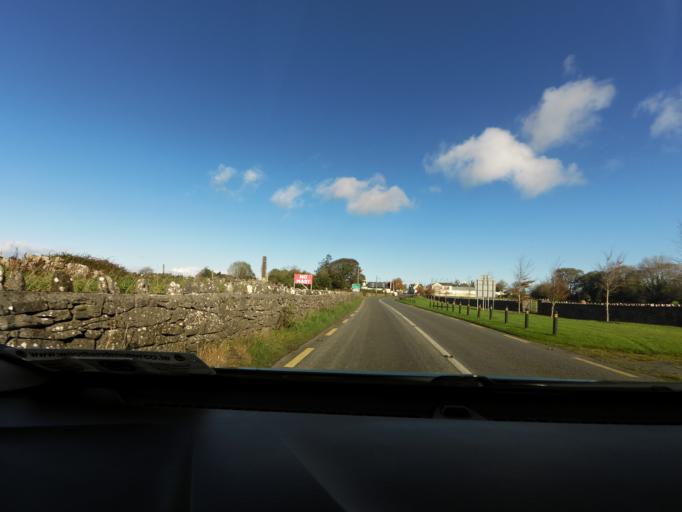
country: IE
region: Connaught
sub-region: Maigh Eo
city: Ballinrobe
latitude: 53.5772
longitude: -9.1225
